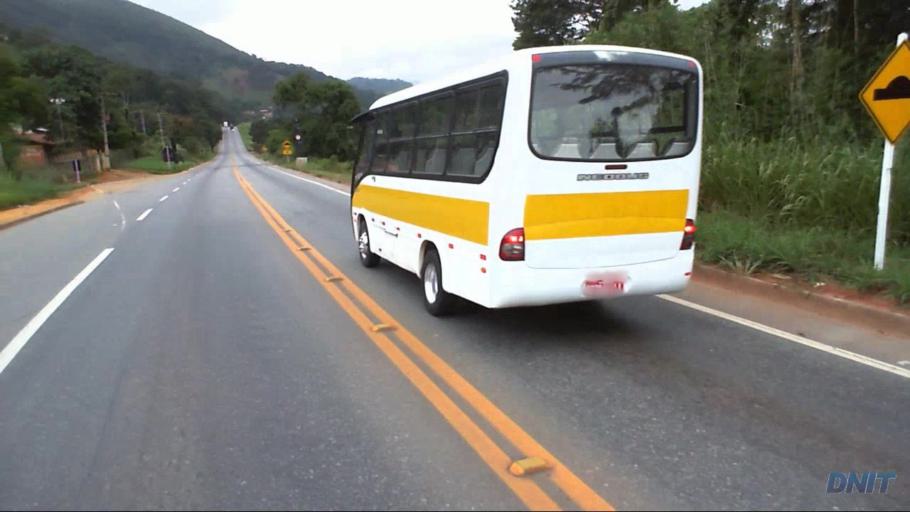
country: BR
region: Minas Gerais
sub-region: Nova Era
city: Nova Era
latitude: -19.7400
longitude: -43.0194
